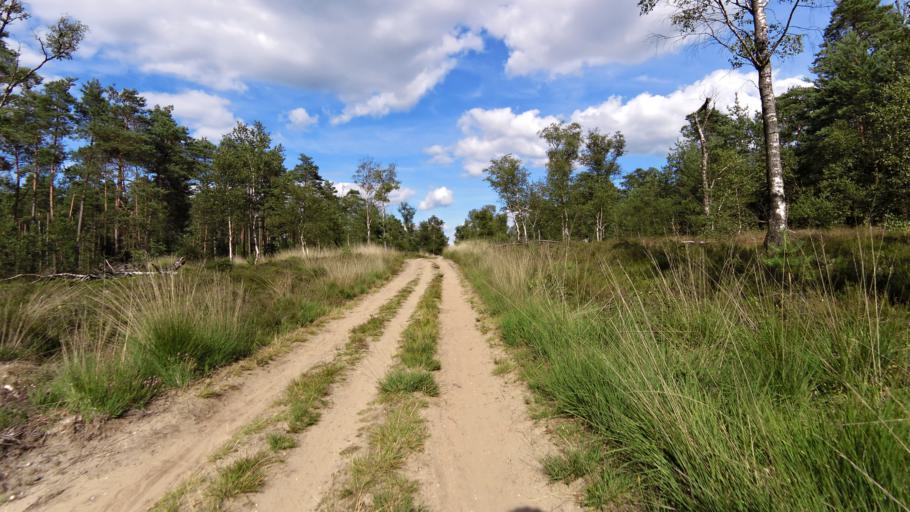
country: NL
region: Gelderland
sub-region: Gemeente Epe
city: Vaassen
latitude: 52.2887
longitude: 5.8850
